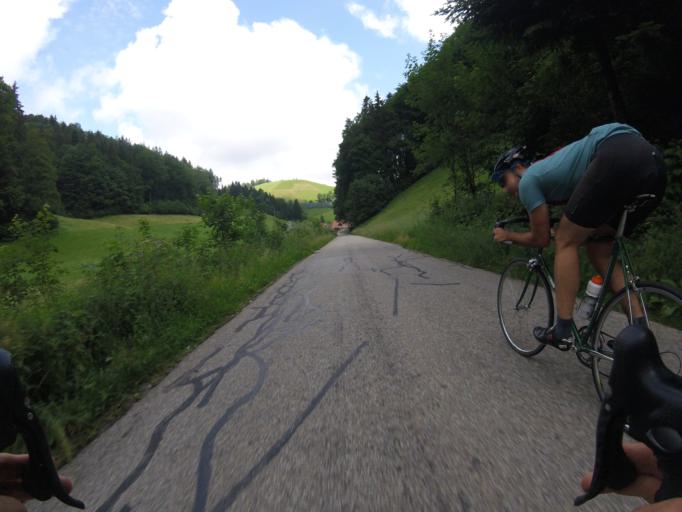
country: CH
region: Bern
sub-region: Emmental District
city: Krauchthal
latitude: 46.9871
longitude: 7.5824
